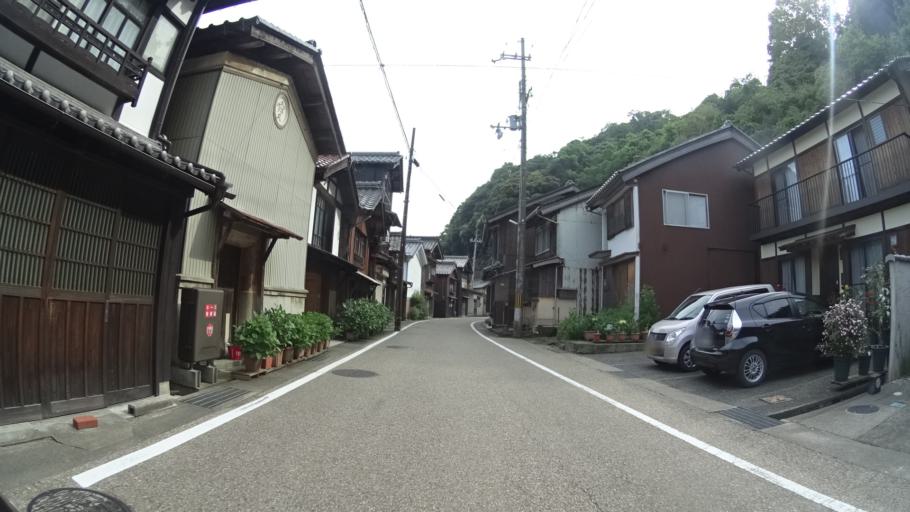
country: JP
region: Kyoto
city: Miyazu
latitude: 35.6713
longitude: 135.2837
